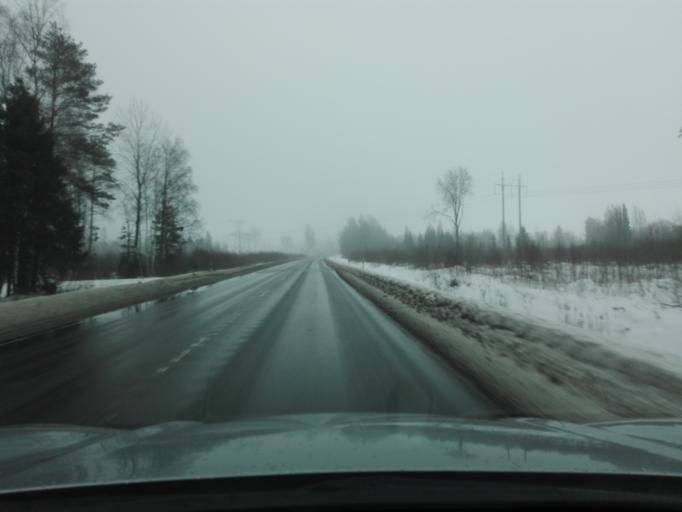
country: EE
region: Raplamaa
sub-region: Kohila vald
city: Kohila
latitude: 59.2355
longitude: 24.7667
